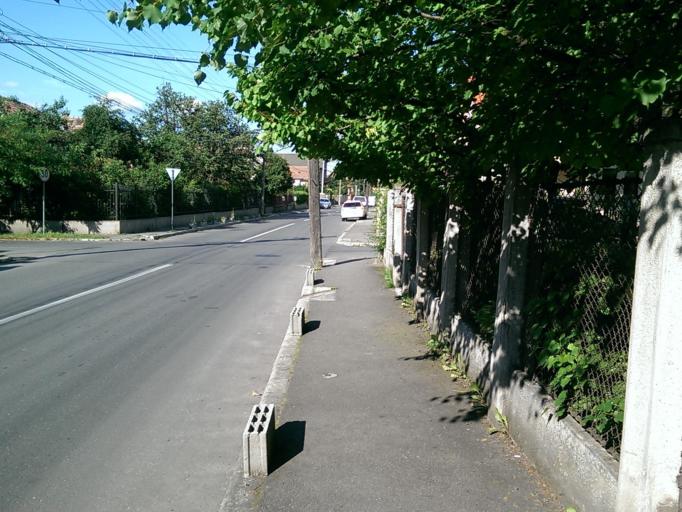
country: RO
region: Cluj
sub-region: Municipiul Cluj-Napoca
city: Cluj-Napoca
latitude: 46.7646
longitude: 23.6076
